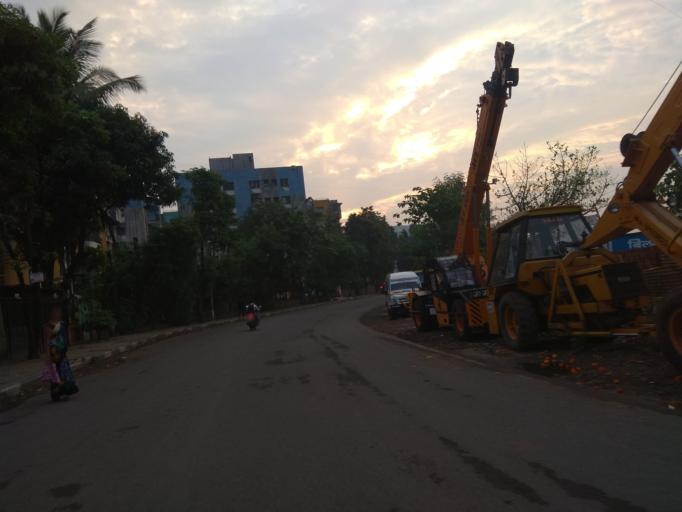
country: IN
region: Maharashtra
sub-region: Pune Division
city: Kharakvasla
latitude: 18.4836
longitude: 73.8034
